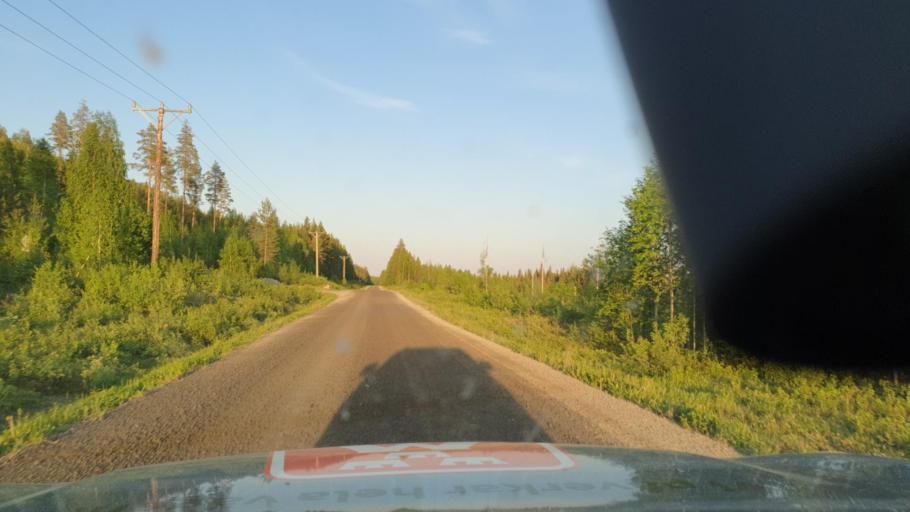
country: SE
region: Norrbotten
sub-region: Bodens Kommun
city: Boden
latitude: 66.0701
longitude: 21.7100
